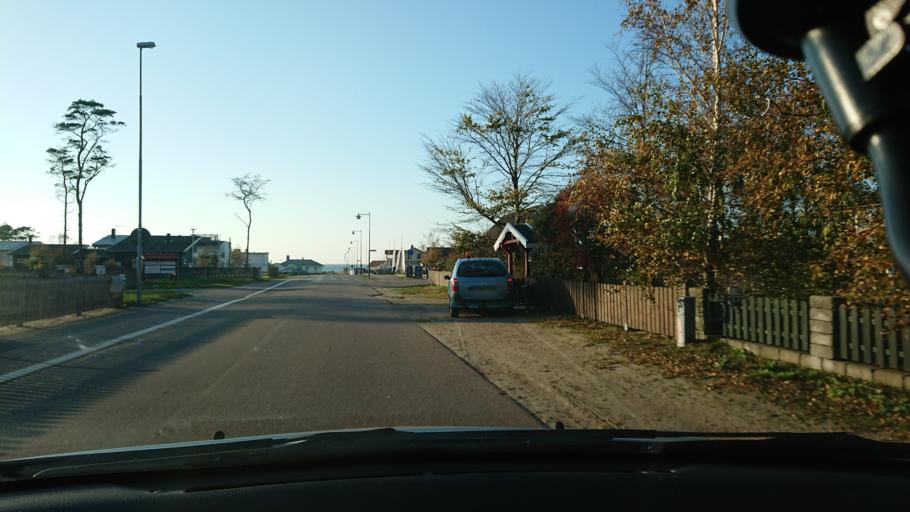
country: SE
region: Halland
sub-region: Laholms Kommun
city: Mellbystrand
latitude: 56.4614
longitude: 12.9202
